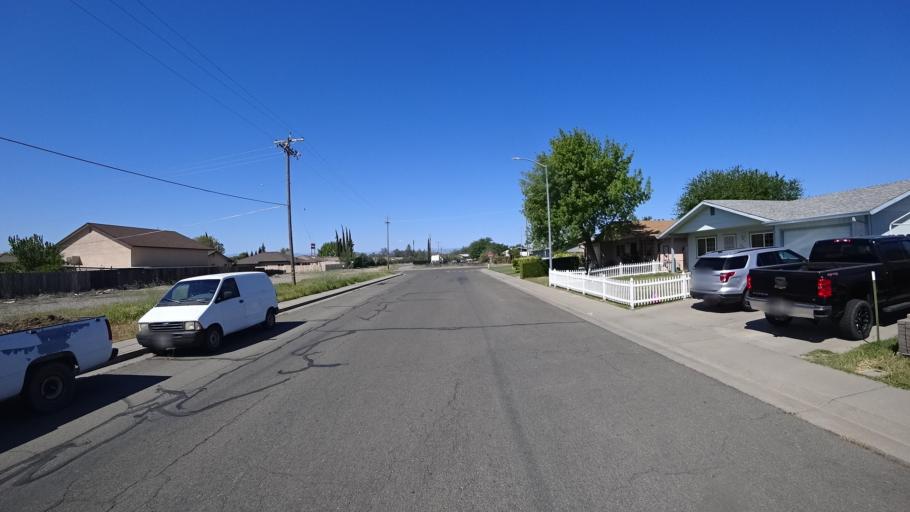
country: US
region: California
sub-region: Glenn County
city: Orland
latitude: 39.7547
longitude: -122.2006
